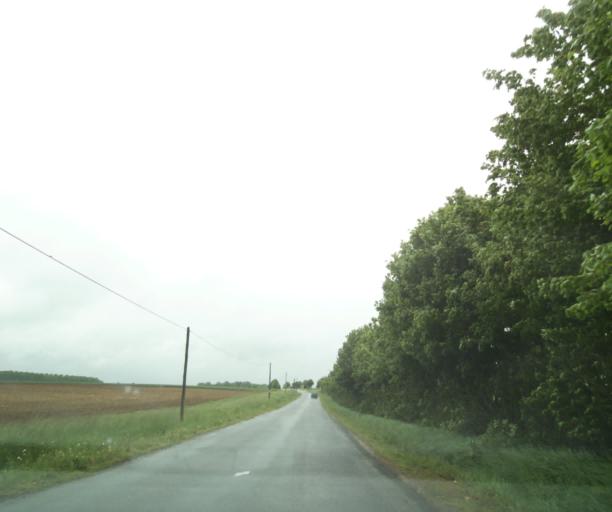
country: FR
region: Poitou-Charentes
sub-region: Departement de la Charente-Maritime
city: Corme-Royal
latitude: 45.7064
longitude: -0.7904
